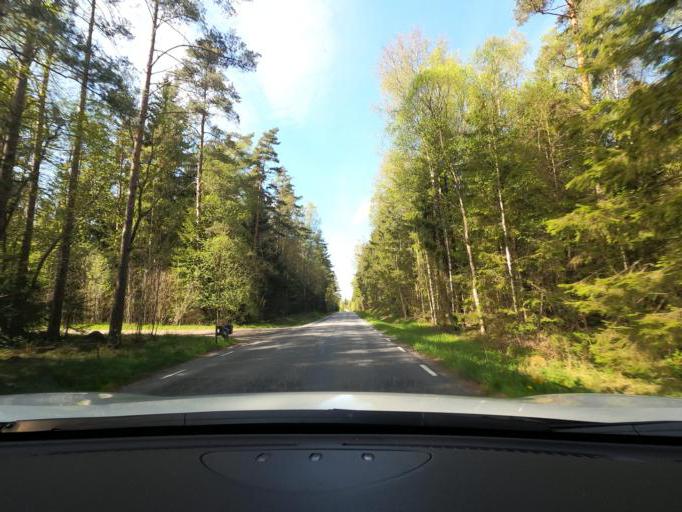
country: SE
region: Vaestra Goetaland
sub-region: Marks Kommun
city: Kinna
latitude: 57.4823
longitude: 12.5670
